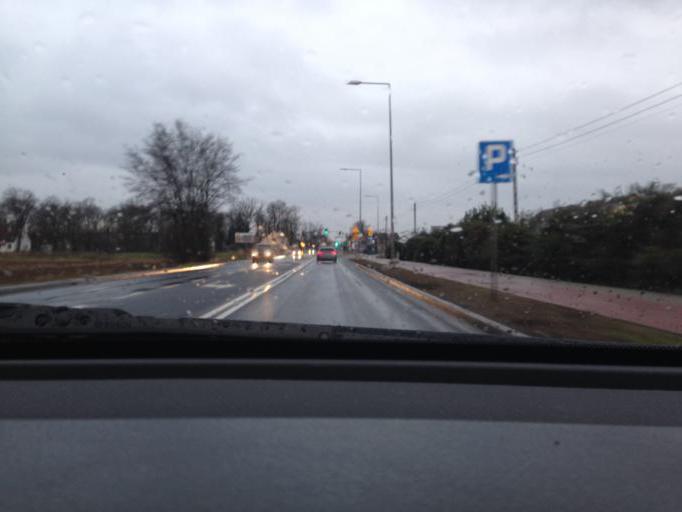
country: PL
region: Opole Voivodeship
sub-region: Powiat opolski
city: Wegry
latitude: 50.7154
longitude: 17.9963
